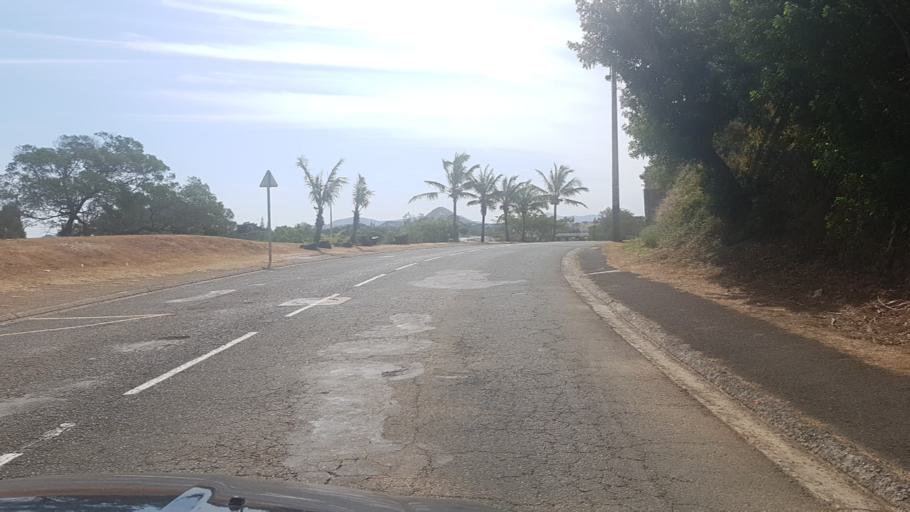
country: NC
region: South Province
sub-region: Noumea
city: Noumea
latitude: -22.2150
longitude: 166.4678
